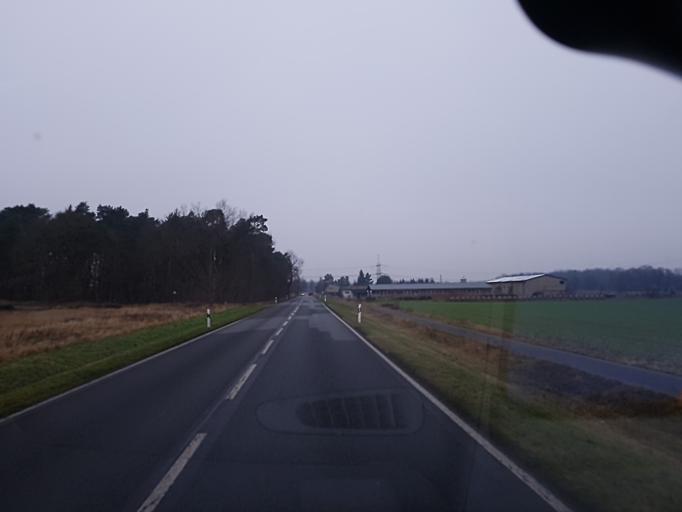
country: DE
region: Brandenburg
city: Lubbenau
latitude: 51.8788
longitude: 13.9086
